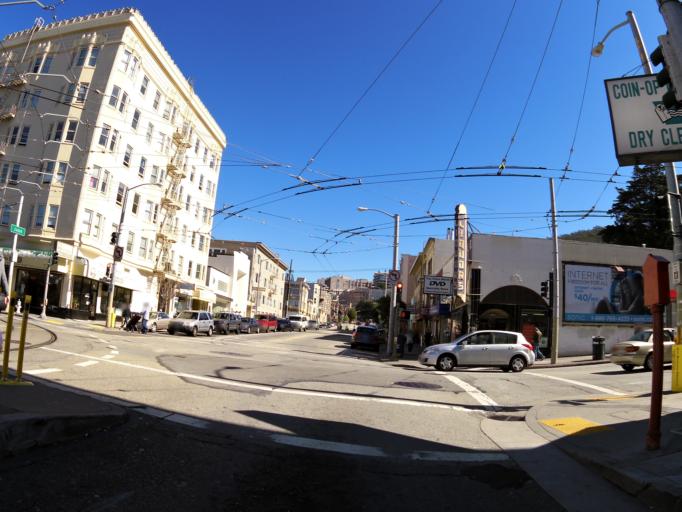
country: US
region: California
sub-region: San Francisco County
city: San Francisco
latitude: 37.7624
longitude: -122.4661
